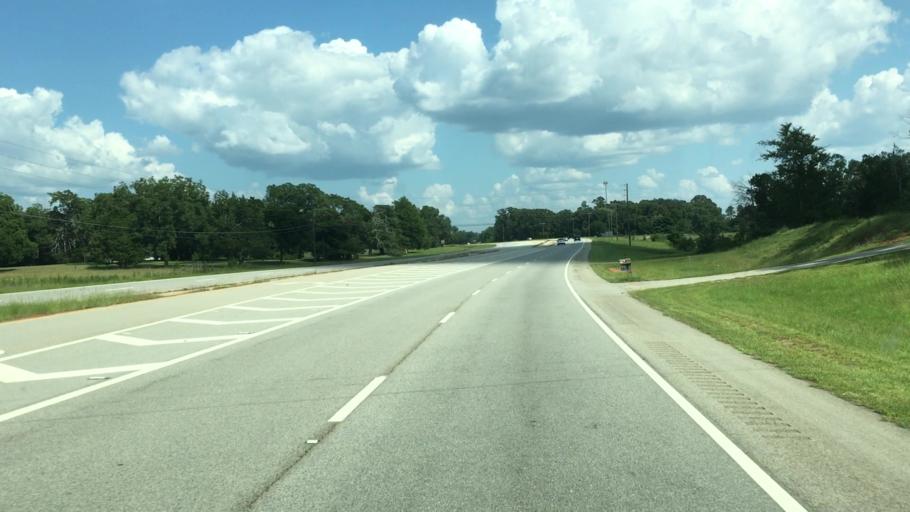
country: US
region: Georgia
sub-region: Putnam County
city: Eatonton
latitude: 33.2717
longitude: -83.3468
